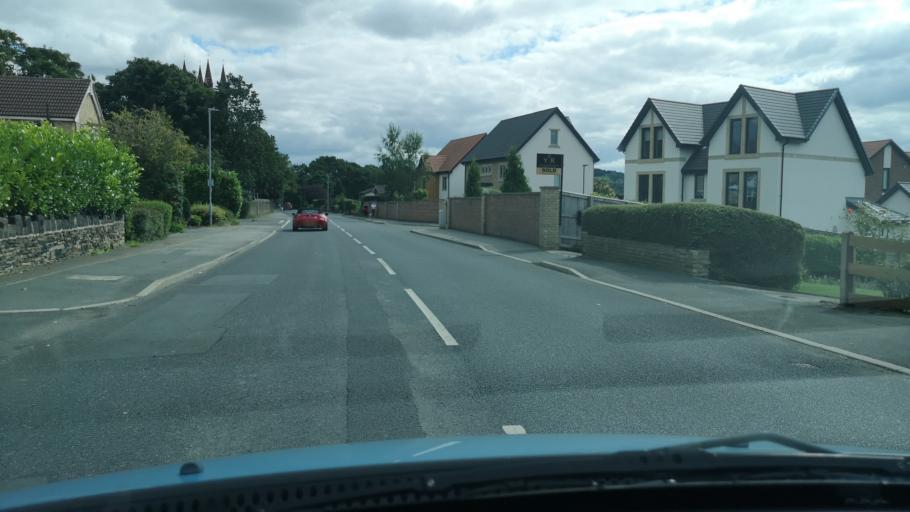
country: GB
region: England
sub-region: Kirklees
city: Mirfield
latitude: 53.6812
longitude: -1.6842
